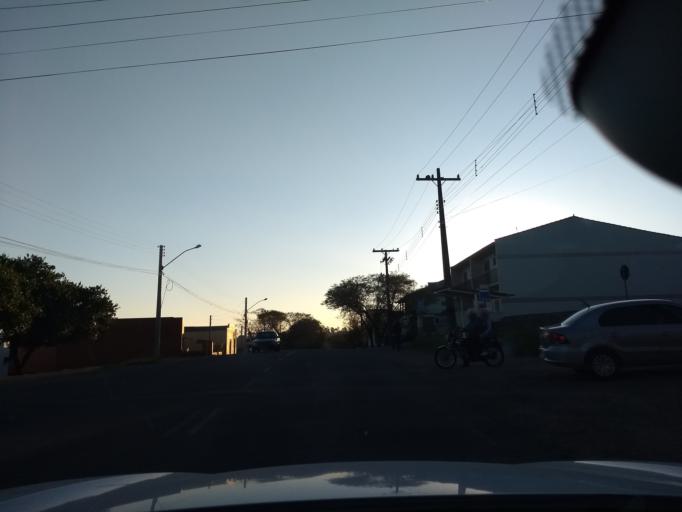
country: BR
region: Rio Grande do Sul
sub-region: Santa Cruz Do Sul
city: Santa Cruz do Sul
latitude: -29.7154
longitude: -52.5129
